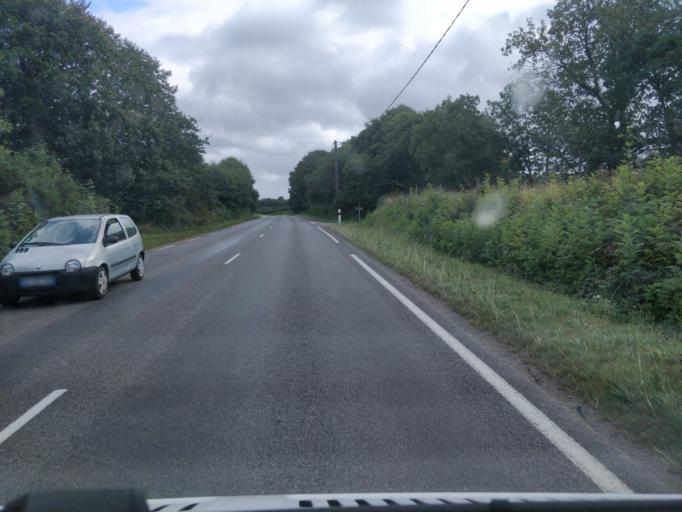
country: FR
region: Brittany
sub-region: Departement du Finistere
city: Ploneis
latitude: 47.9923
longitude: -4.2227
